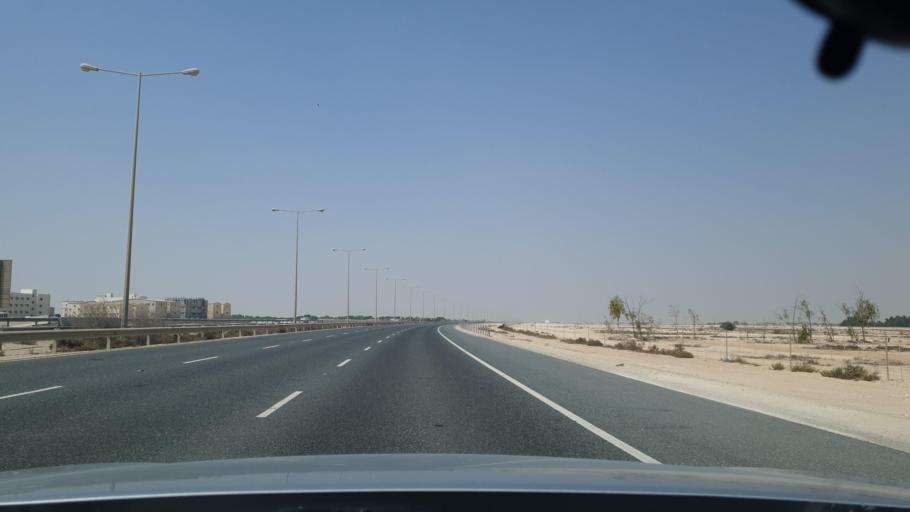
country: QA
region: Al Khawr
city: Al Khawr
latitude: 25.7578
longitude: 51.4276
